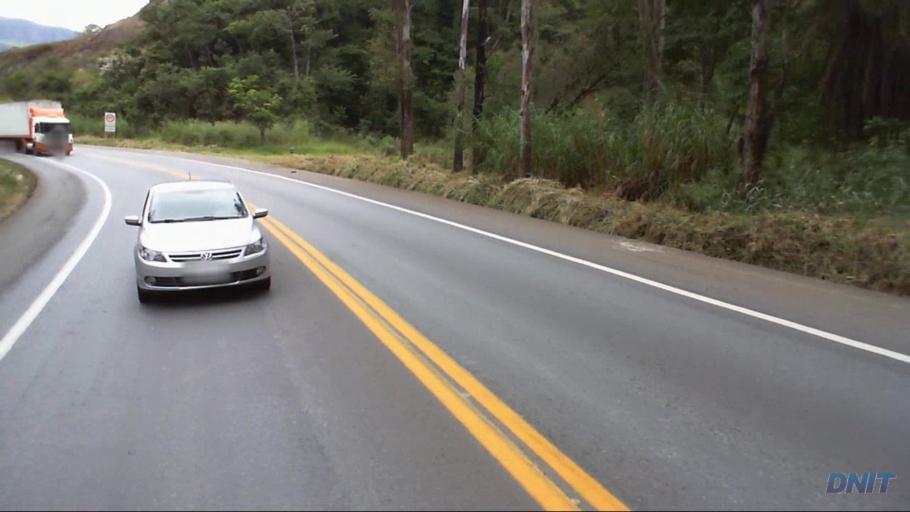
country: BR
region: Minas Gerais
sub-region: Joao Monlevade
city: Joao Monlevade
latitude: -19.8574
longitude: -43.2379
